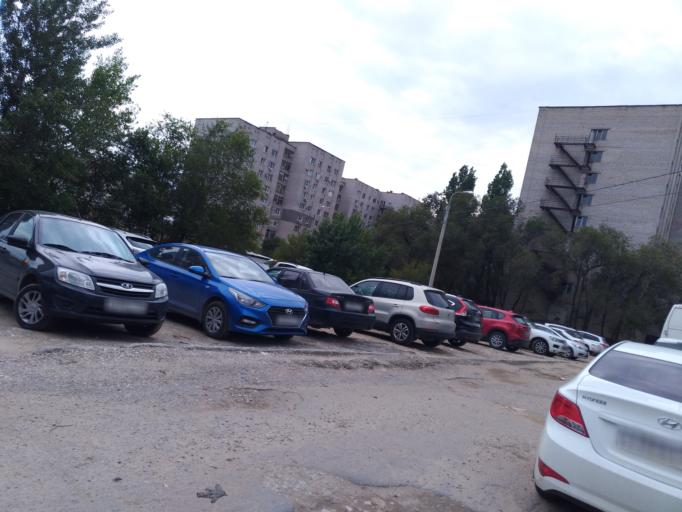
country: RU
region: Volgograd
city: Volgograd
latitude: 48.7292
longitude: 44.5243
